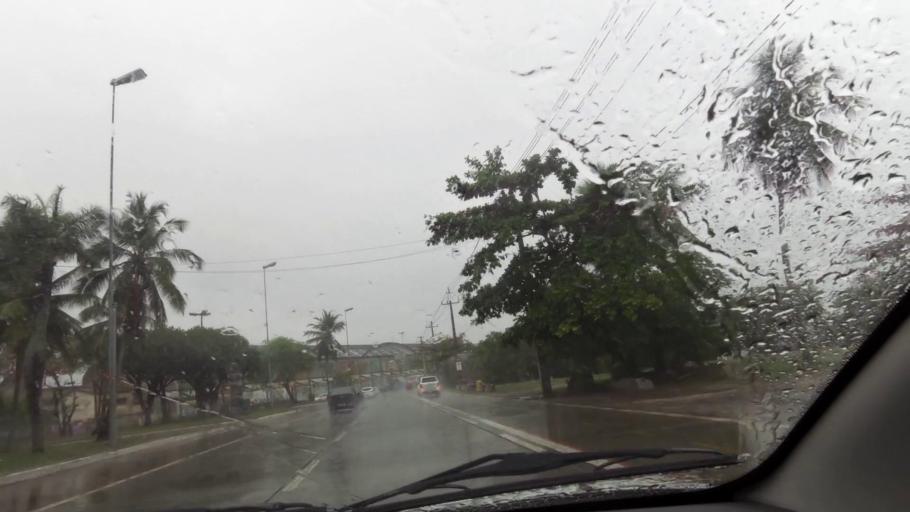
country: BR
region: Pernambuco
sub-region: Recife
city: Recife
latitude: -8.0780
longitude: -34.8912
